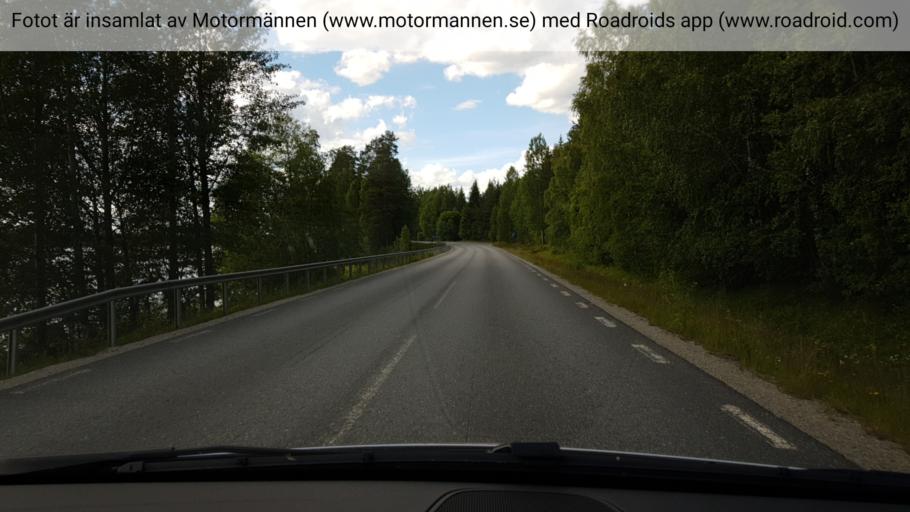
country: SE
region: Jaemtland
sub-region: Braecke Kommun
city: Braecke
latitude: 62.3942
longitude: 15.0370
